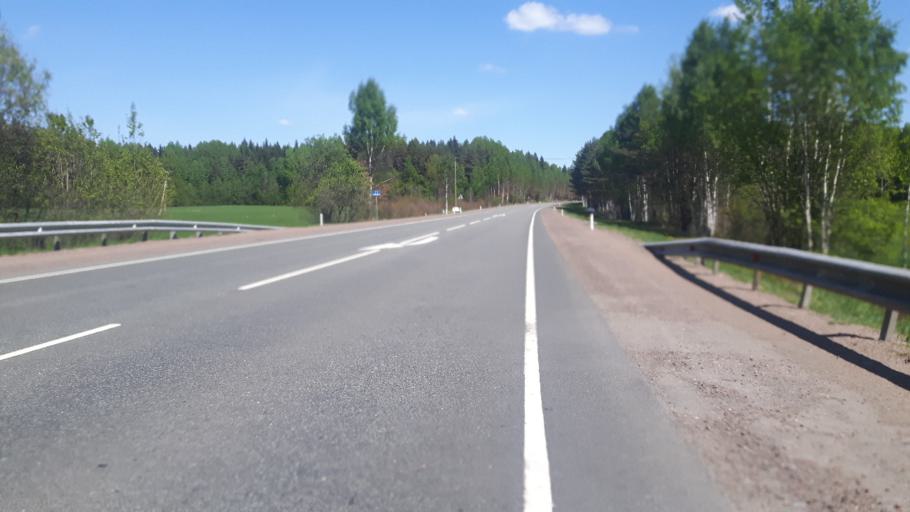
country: RU
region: Leningrad
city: Vysotsk
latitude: 60.6337
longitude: 28.2740
